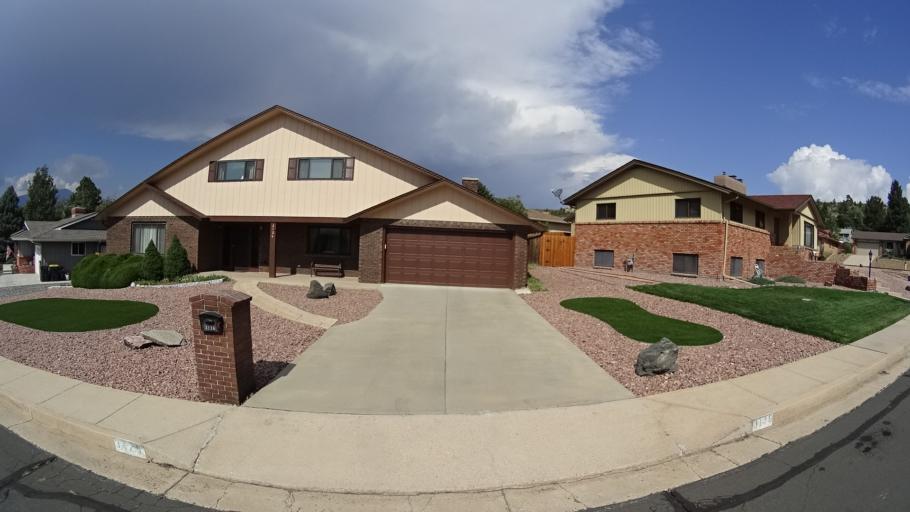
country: US
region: Colorado
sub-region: El Paso County
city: Colorado Springs
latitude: 38.8671
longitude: -104.7707
